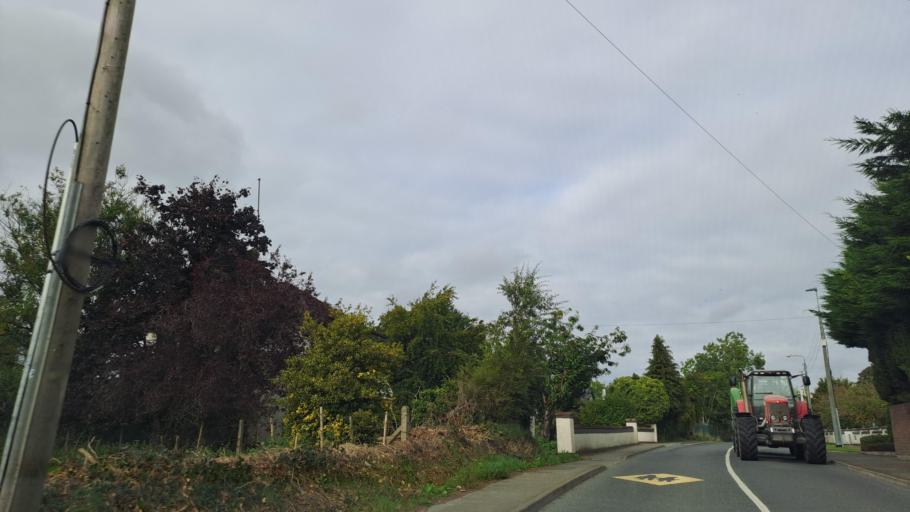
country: IE
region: Ulster
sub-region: An Cabhan
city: Bailieborough
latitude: 53.9917
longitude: -6.8924
